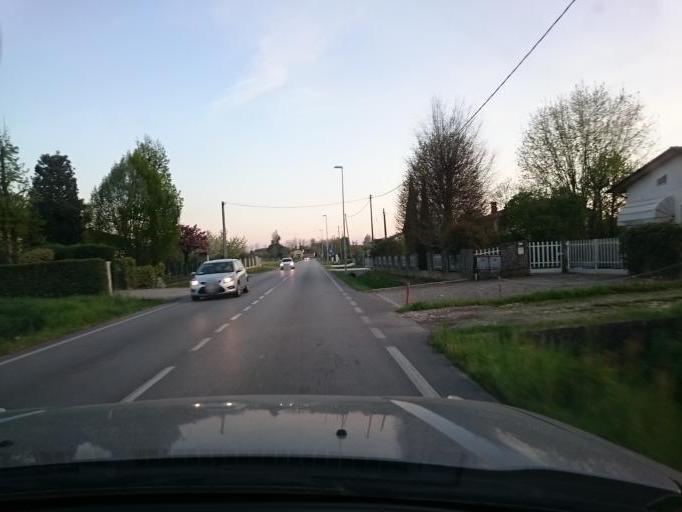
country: IT
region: Veneto
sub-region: Provincia di Treviso
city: Badoere
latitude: 45.6440
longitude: 12.1047
